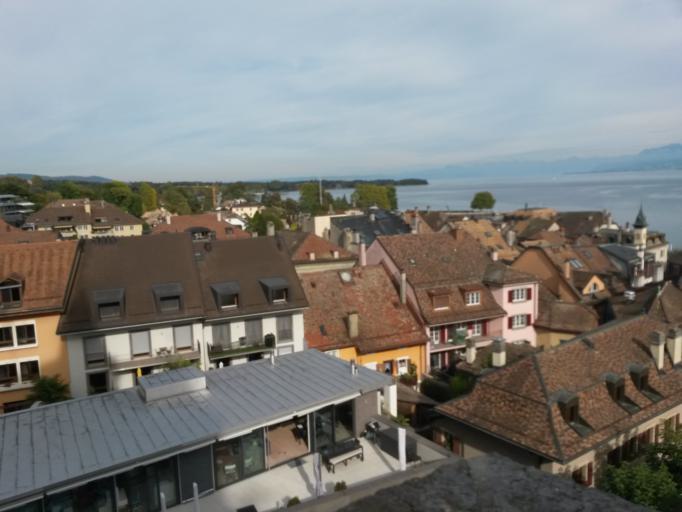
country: CH
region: Vaud
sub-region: Nyon District
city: Nyon
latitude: 46.3821
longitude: 6.2410
